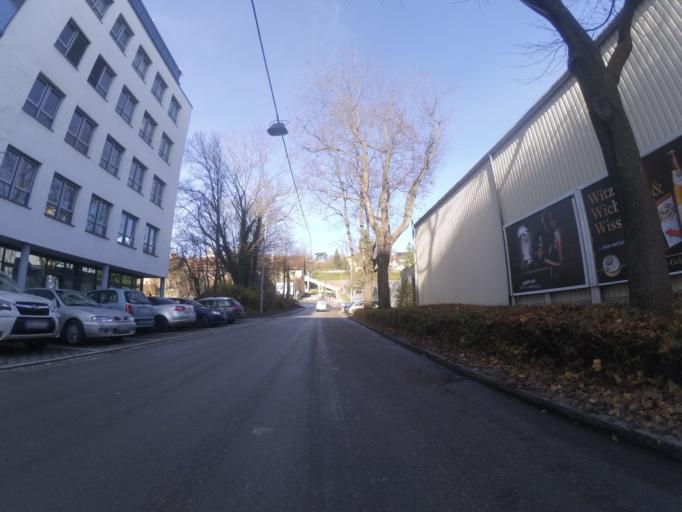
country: DE
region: Baden-Wuerttemberg
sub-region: Tuebingen Region
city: Ulm
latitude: 48.4060
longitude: 9.9892
